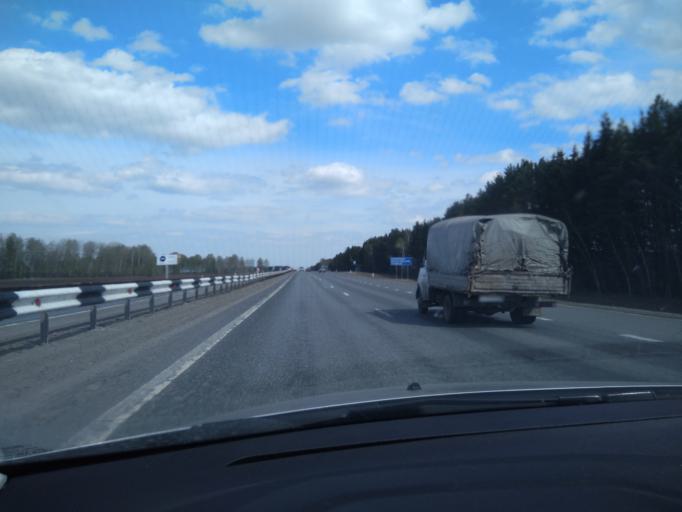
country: RU
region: Tjumen
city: Moskovskiy
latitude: 57.0965
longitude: 65.2364
